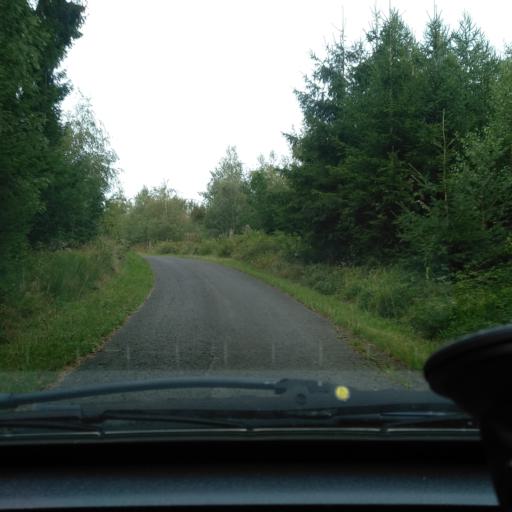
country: DE
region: Hesse
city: Dillenburg
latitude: 50.8024
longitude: 8.3233
